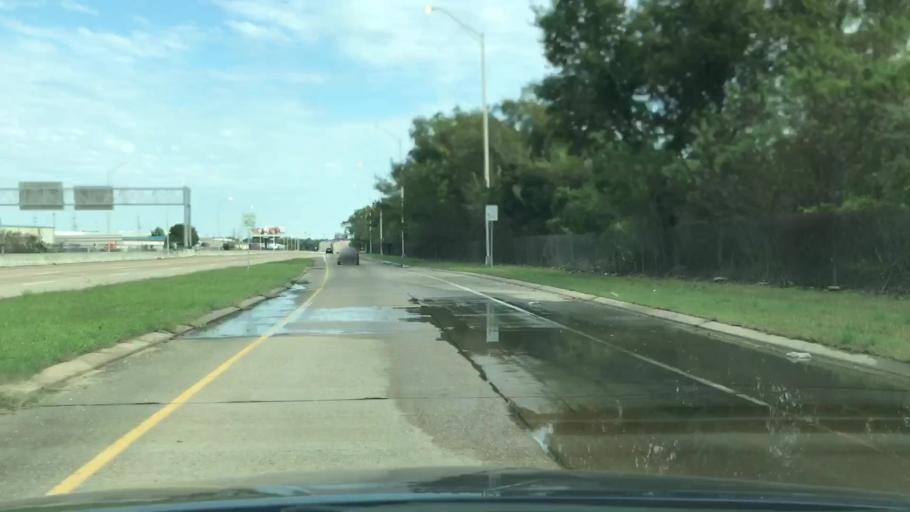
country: US
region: Louisiana
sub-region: Jefferson Parish
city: Jefferson
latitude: 29.9695
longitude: -90.1415
